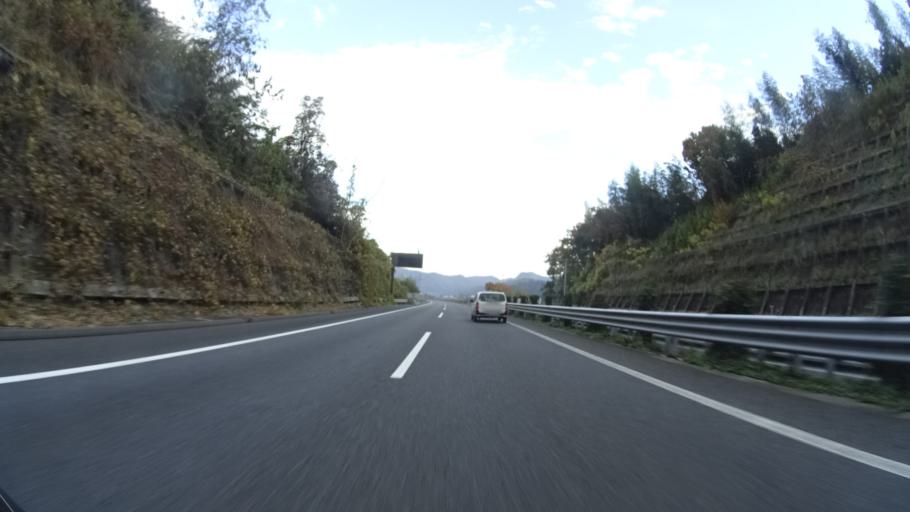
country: JP
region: Tochigi
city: Ashikaga
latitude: 36.3652
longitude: 139.4758
